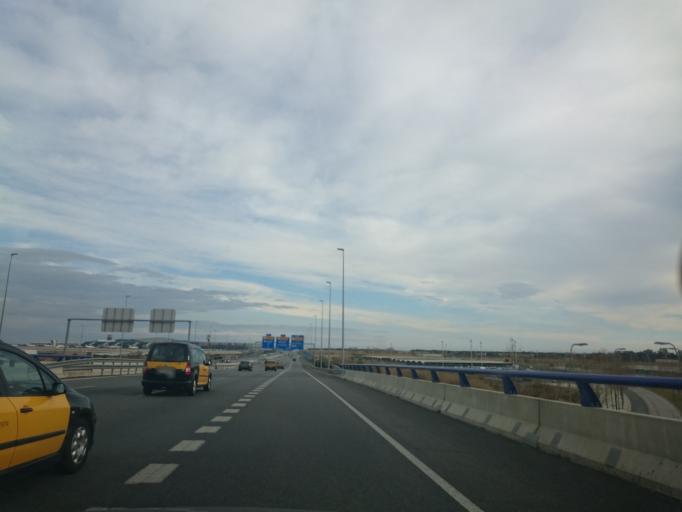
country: ES
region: Catalonia
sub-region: Provincia de Barcelona
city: Viladecans
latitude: 41.2948
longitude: 2.0523
